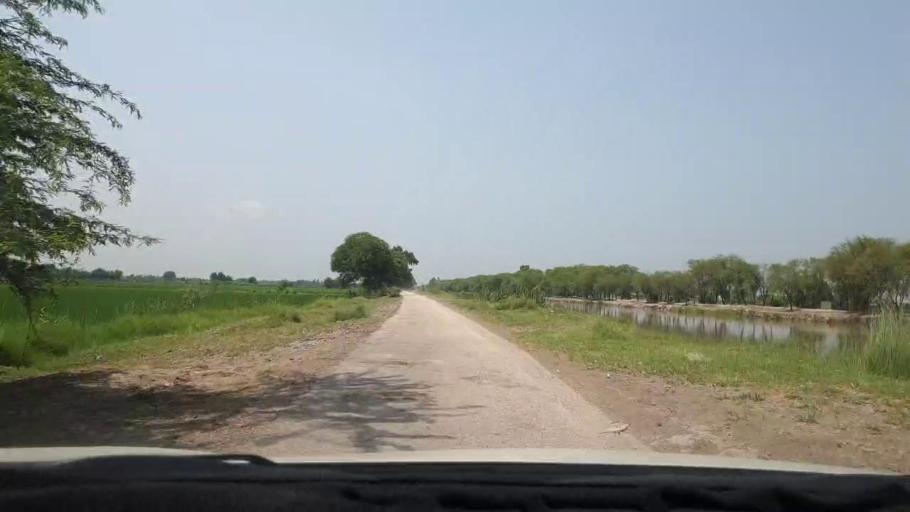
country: PK
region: Sindh
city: Dokri
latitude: 27.3108
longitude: 68.0996
